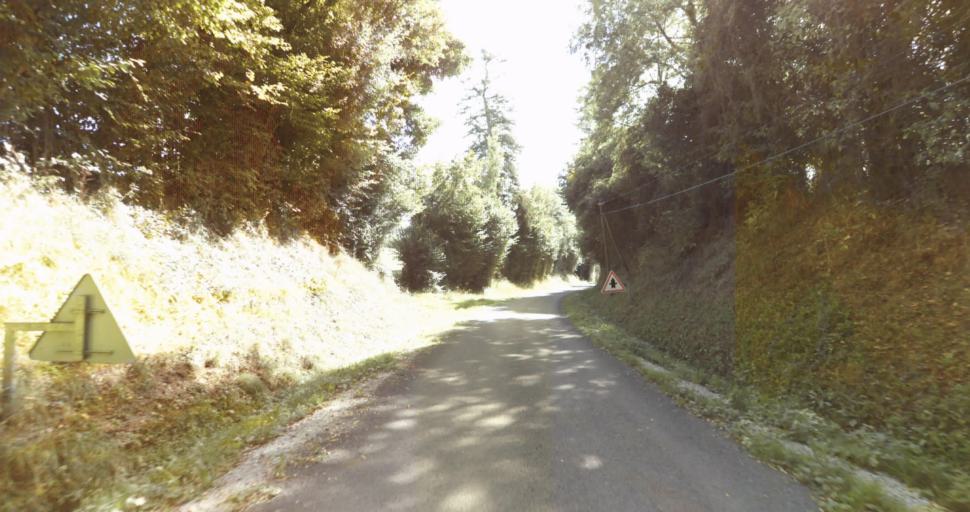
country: FR
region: Lower Normandy
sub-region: Departement de l'Orne
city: Gace
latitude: 48.7378
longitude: 0.2395
